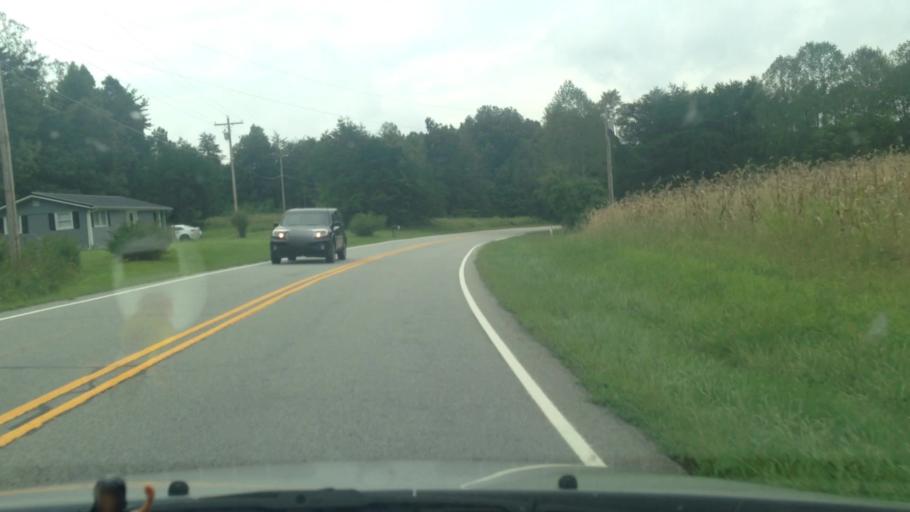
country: US
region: North Carolina
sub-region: Stokes County
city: Danbury
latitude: 36.4098
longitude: -80.1136
